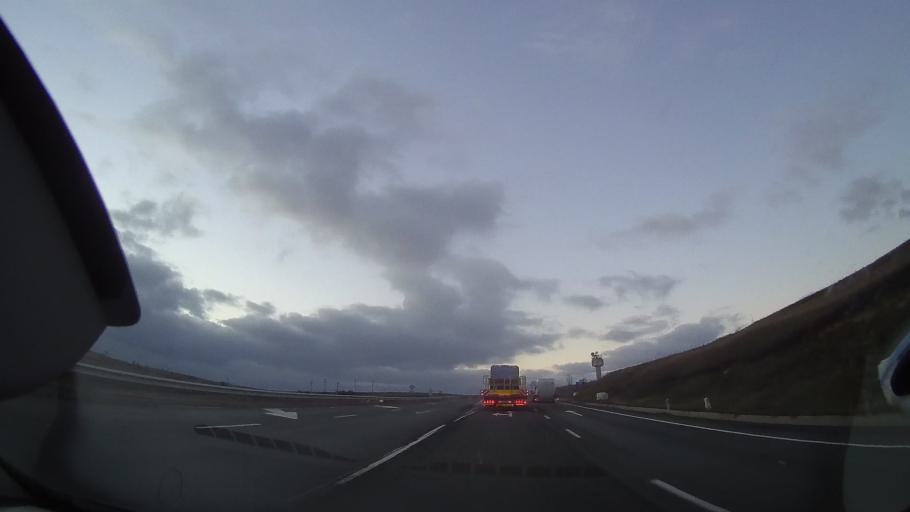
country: RO
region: Cluj
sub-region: Comuna Izvoru Crisului
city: Izvoru Crisului
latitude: 46.8239
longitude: 23.1583
